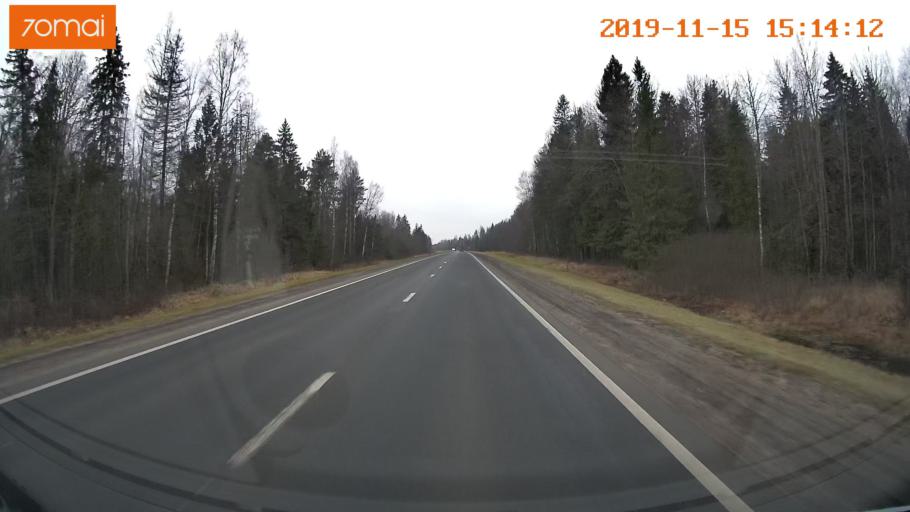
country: RU
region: Jaroslavl
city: Danilov
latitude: 58.3031
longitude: 40.2083
